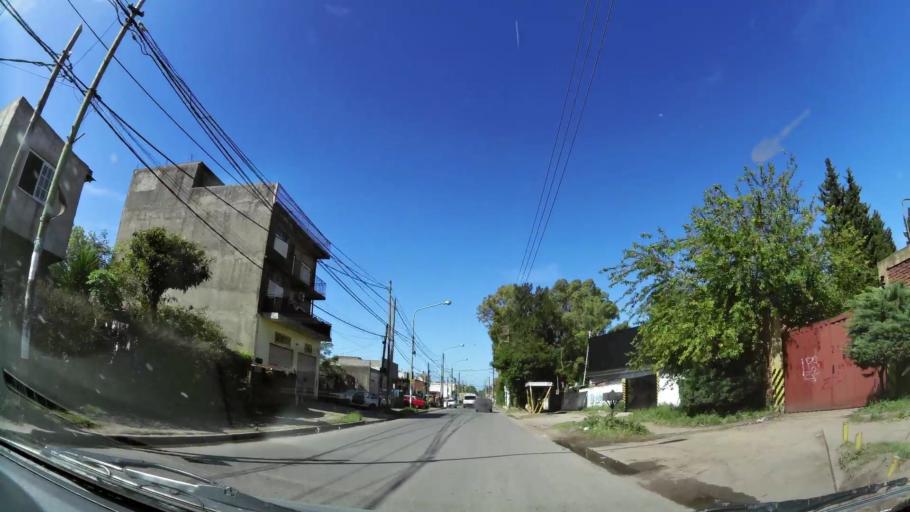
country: AR
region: Buenos Aires
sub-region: Partido de Quilmes
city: Quilmes
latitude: -34.8039
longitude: -58.2453
